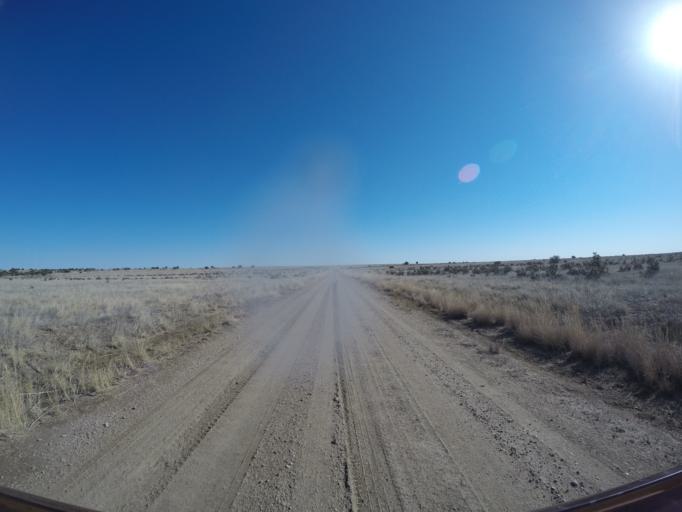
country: US
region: Colorado
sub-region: Otero County
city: La Junta
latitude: 37.6534
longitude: -103.6012
